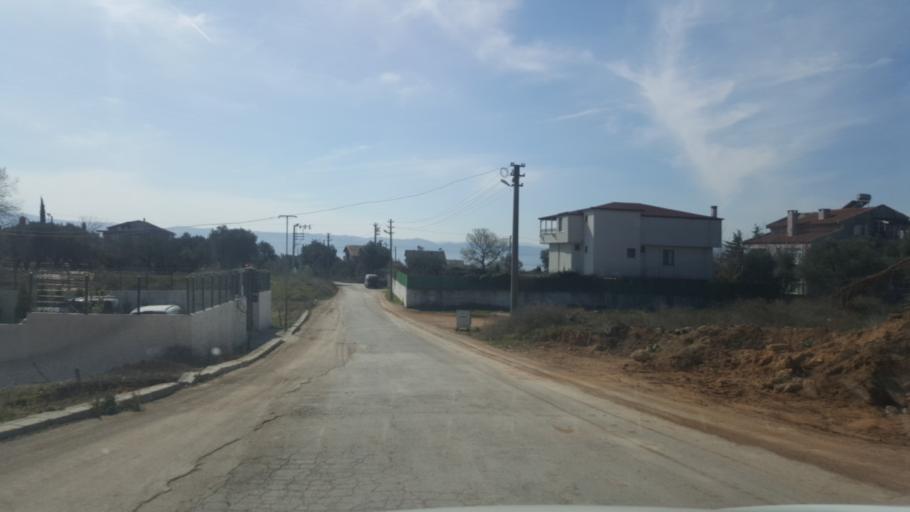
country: TR
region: Kocaeli
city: Tavsancil
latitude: 40.7759
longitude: 29.5717
